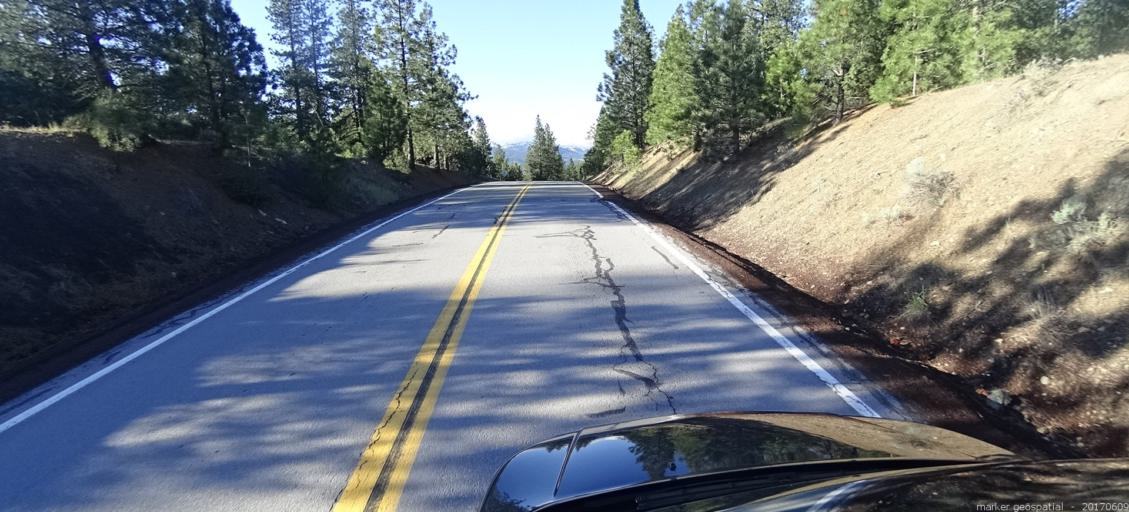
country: US
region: California
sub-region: Siskiyou County
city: Weed
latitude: 41.4362
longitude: -122.6393
